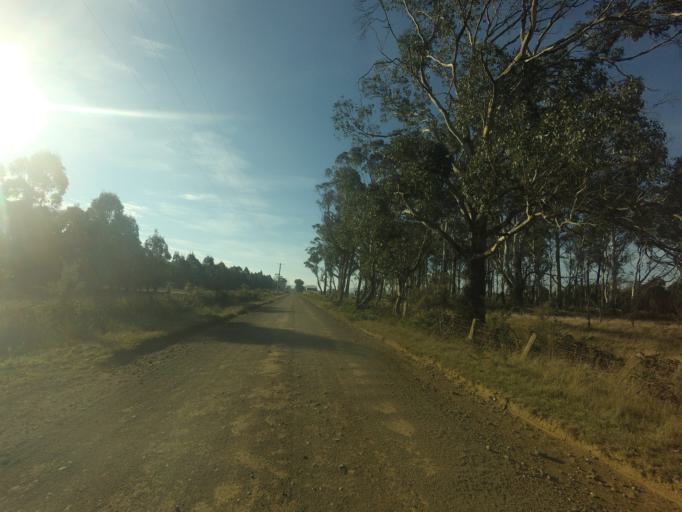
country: AU
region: Tasmania
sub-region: Brighton
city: Bridgewater
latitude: -42.4436
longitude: 147.3857
